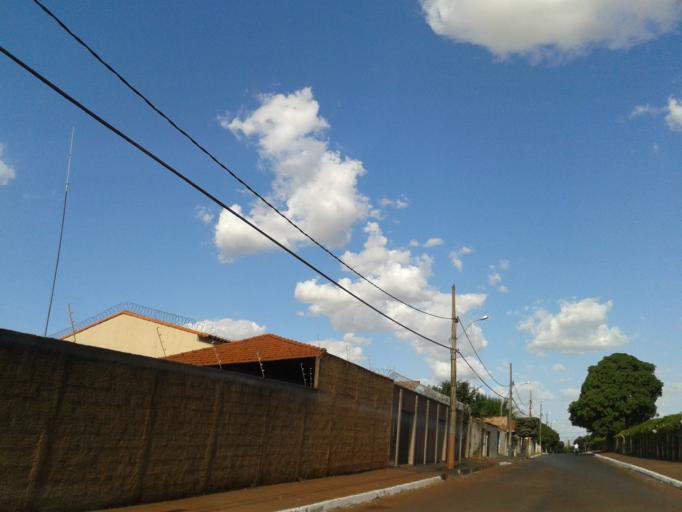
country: BR
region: Minas Gerais
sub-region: Capinopolis
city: Capinopolis
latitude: -18.6928
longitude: -49.5656
